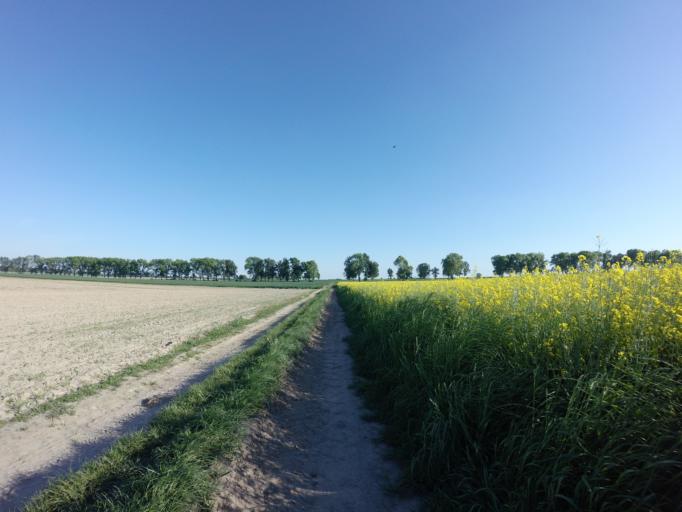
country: PL
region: West Pomeranian Voivodeship
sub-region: Powiat choszczenski
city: Choszczno
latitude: 53.1304
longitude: 15.3902
